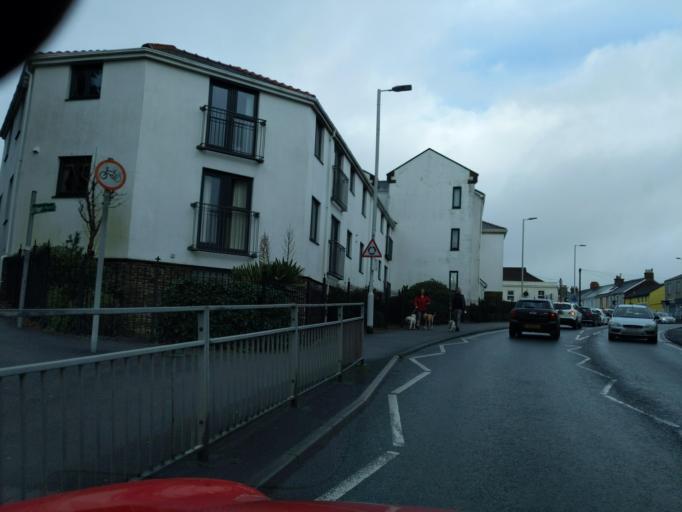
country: GB
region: England
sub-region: Devon
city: Plympton
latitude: 50.3870
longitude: -4.0511
